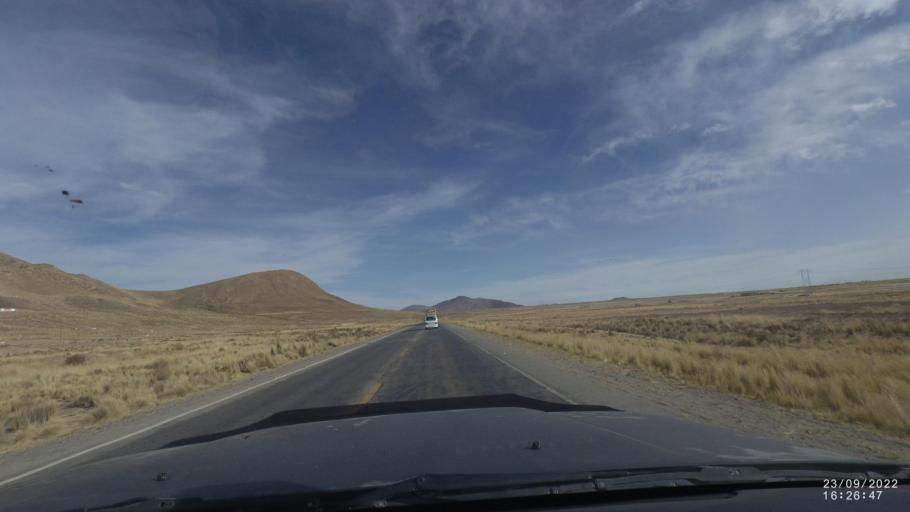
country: BO
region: Oruro
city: Machacamarca
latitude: -18.1088
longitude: -67.0058
